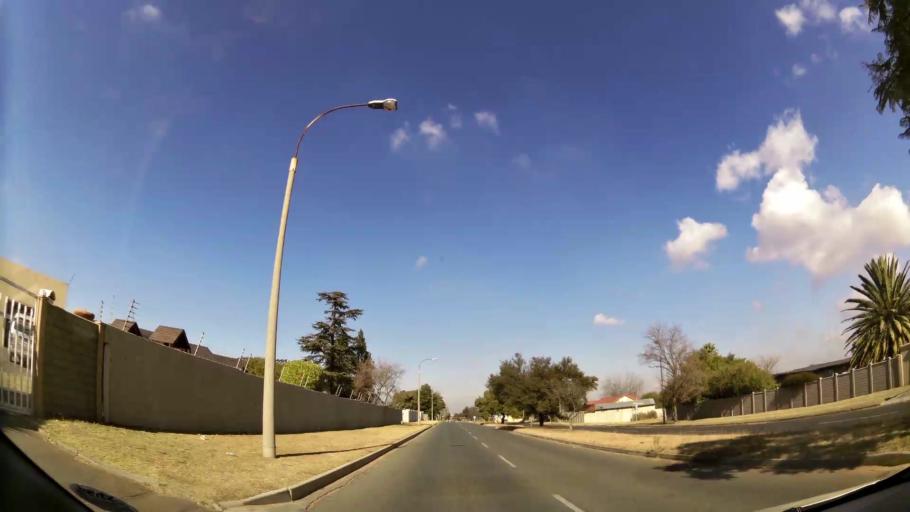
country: ZA
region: Gauteng
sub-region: City of Johannesburg Metropolitan Municipality
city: Roodepoort
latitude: -26.1455
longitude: 27.8250
